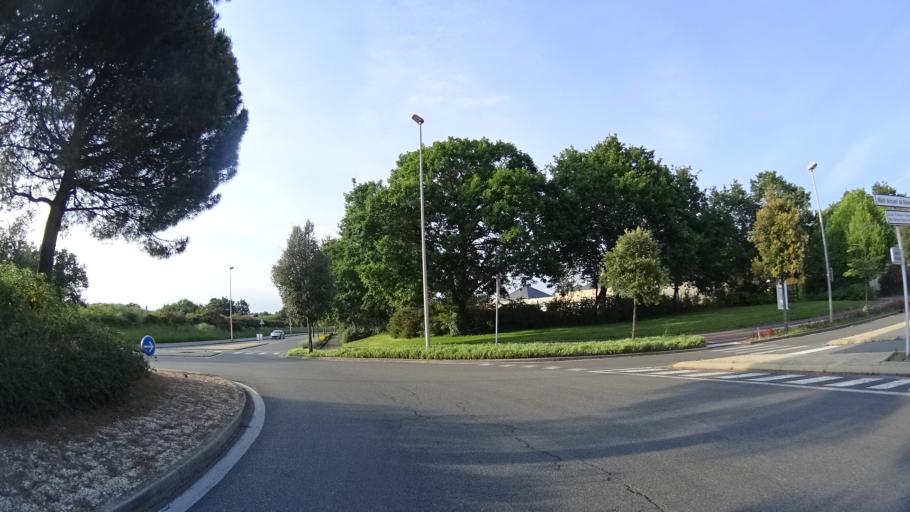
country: FR
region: Brittany
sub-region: Departement du Morbihan
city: Vannes
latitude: 47.6494
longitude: -2.7441
